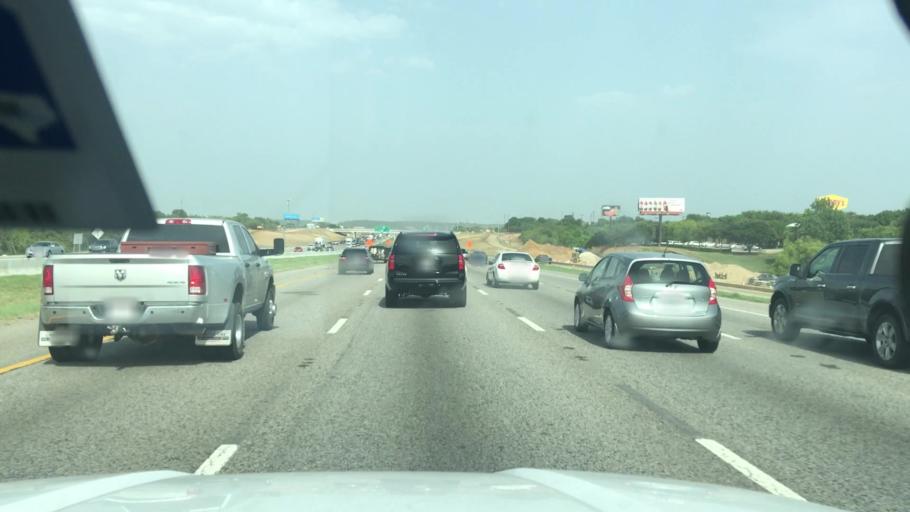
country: US
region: Texas
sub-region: Dallas County
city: Grand Prairie
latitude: 32.6750
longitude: -97.0062
